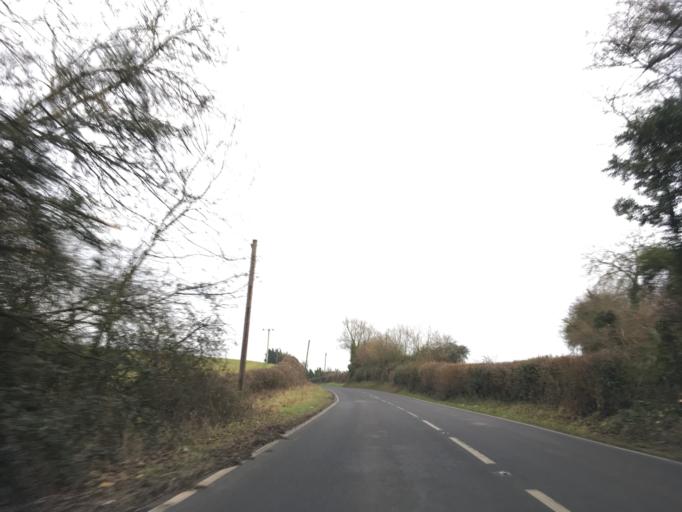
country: GB
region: England
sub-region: South Gloucestershire
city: Pucklechurch
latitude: 51.5107
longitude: -2.4359
